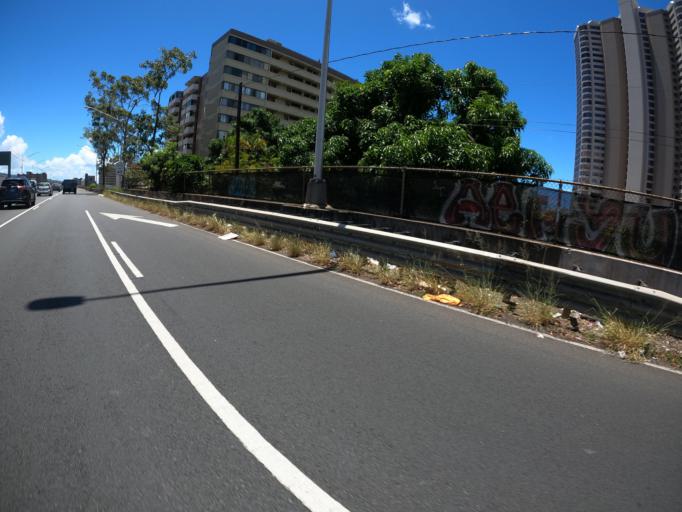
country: US
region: Hawaii
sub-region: Honolulu County
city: Honolulu
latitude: 21.3048
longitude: -157.8464
